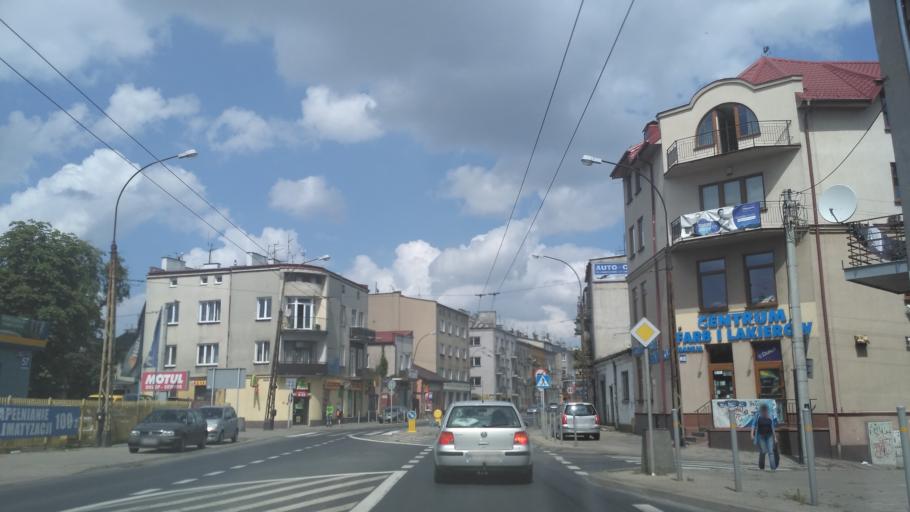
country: PL
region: Lublin Voivodeship
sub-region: Powiat lubelski
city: Lublin
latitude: 51.2257
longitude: 22.5735
